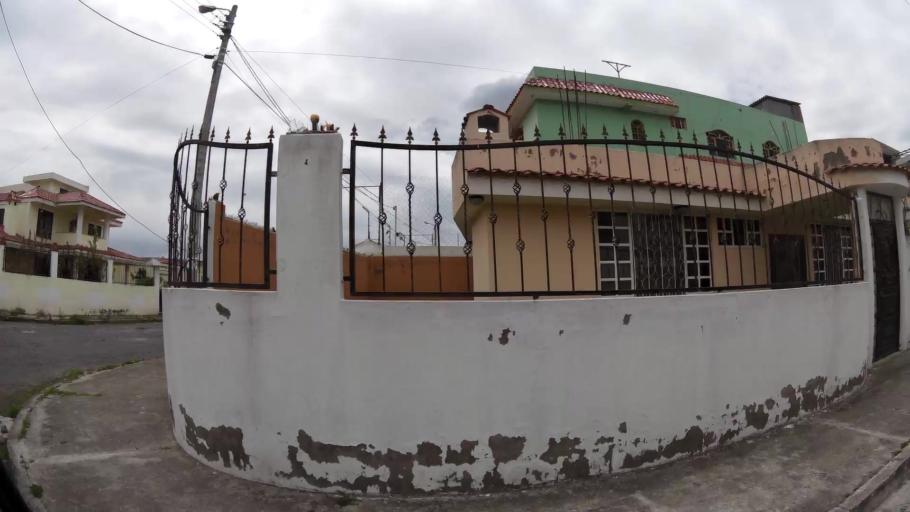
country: EC
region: Cotopaxi
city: Latacunga
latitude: -0.9675
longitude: -78.6134
